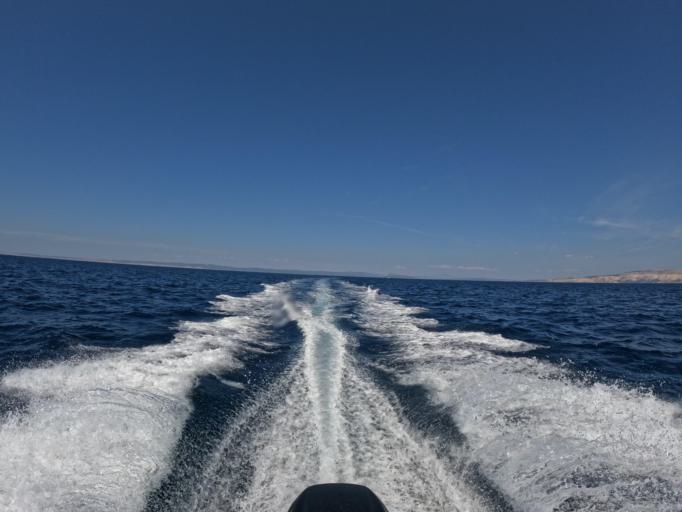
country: HR
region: Primorsko-Goranska
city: Lopar
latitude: 44.8601
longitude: 14.6925
